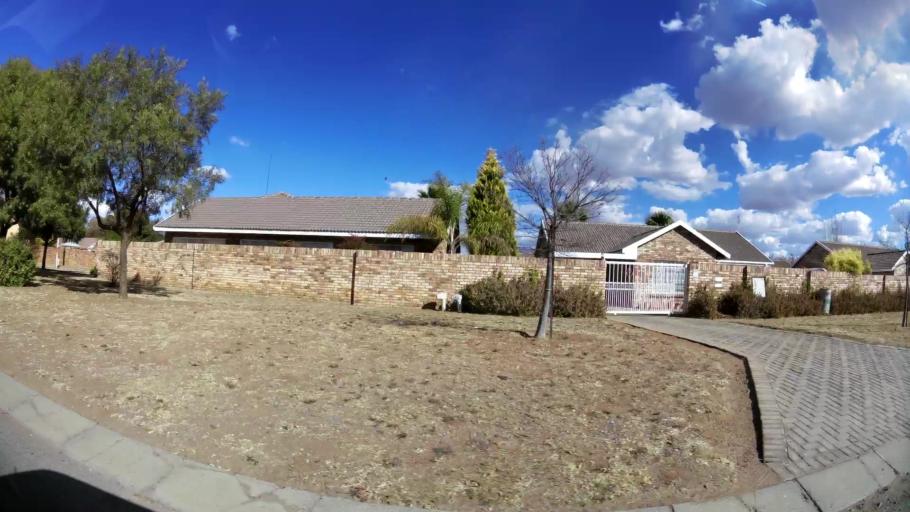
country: ZA
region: North-West
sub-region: Dr Kenneth Kaunda District Municipality
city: Klerksdorp
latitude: -26.8335
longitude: 26.6533
